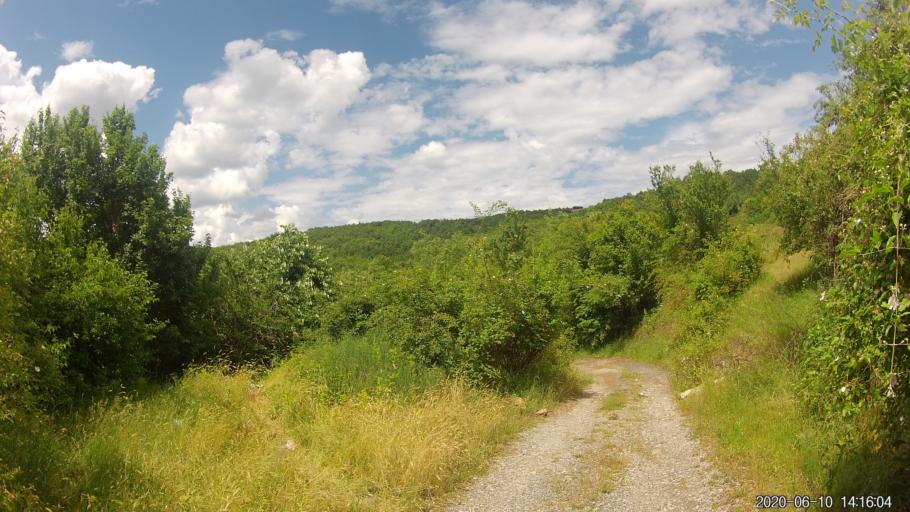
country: XK
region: Prizren
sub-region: Komuna e Therandes
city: Budakovo
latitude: 42.4035
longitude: 20.9257
